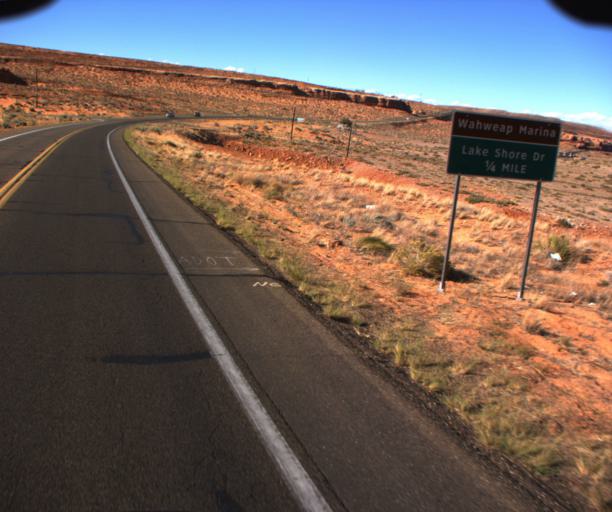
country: US
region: Arizona
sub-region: Coconino County
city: Page
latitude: 36.9369
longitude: -111.4925
